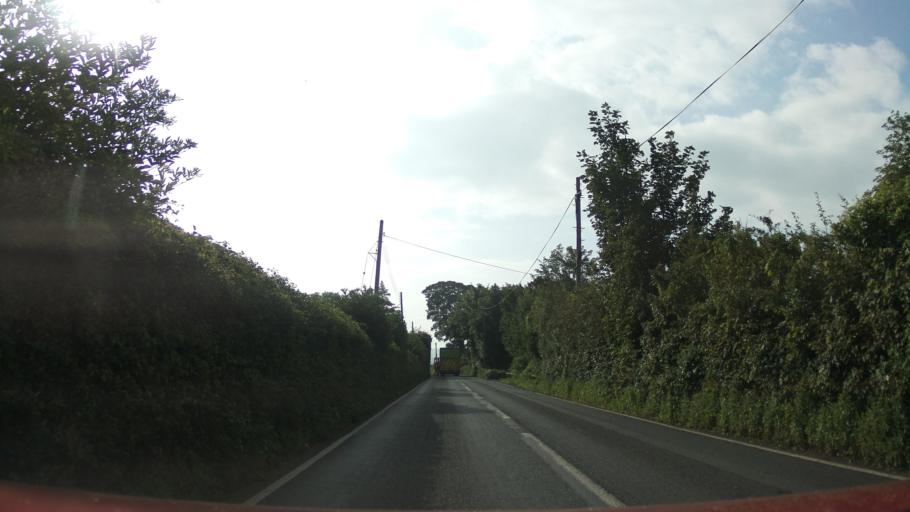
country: GB
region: England
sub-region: North Somerset
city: Nailsea
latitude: 51.4369
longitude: -2.7227
